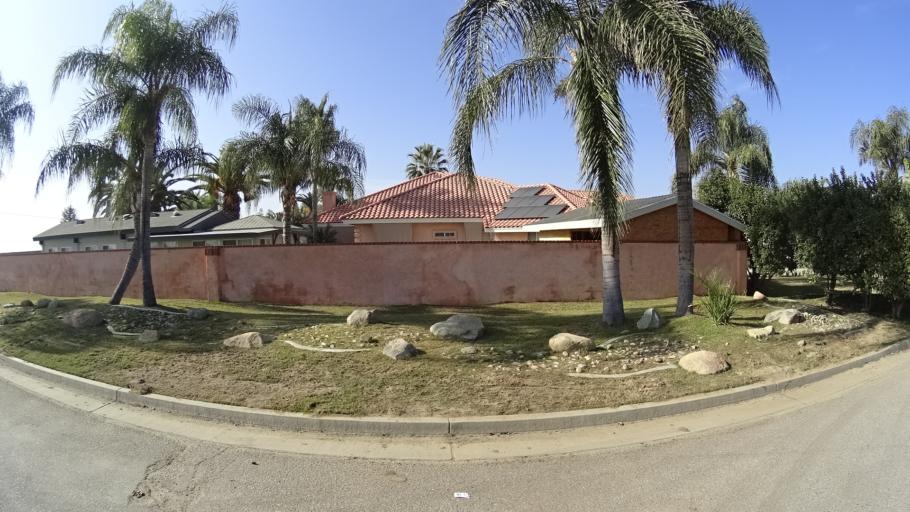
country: US
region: California
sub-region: Kern County
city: Rosedale
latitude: 35.3552
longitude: -119.1899
